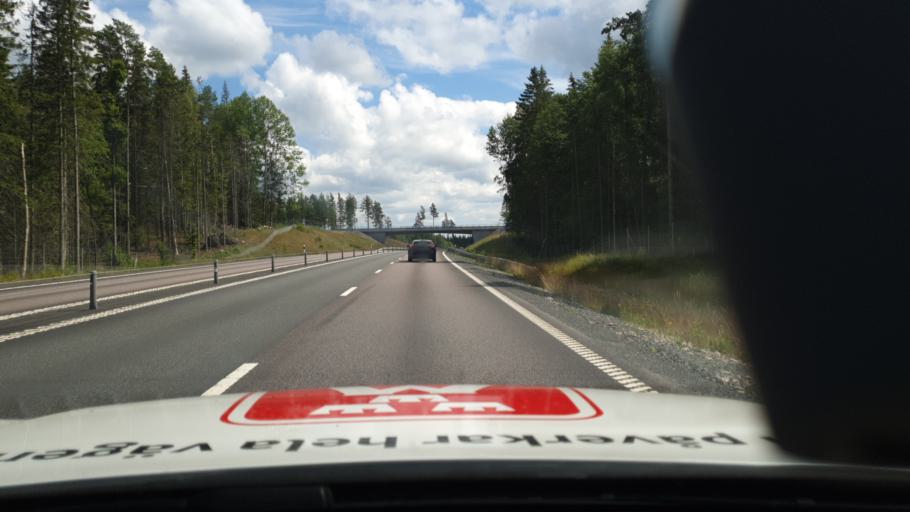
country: SE
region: Joenkoeping
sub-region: Mullsjo Kommun
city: Mullsjoe
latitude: 57.8952
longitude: 13.8776
